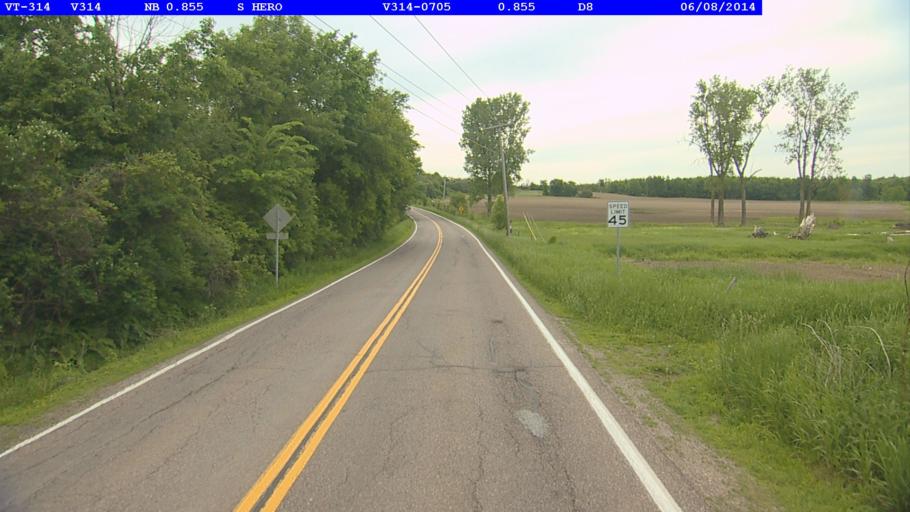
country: US
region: New York
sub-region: Clinton County
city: Cumberland Head
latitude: 44.6707
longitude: -73.3366
